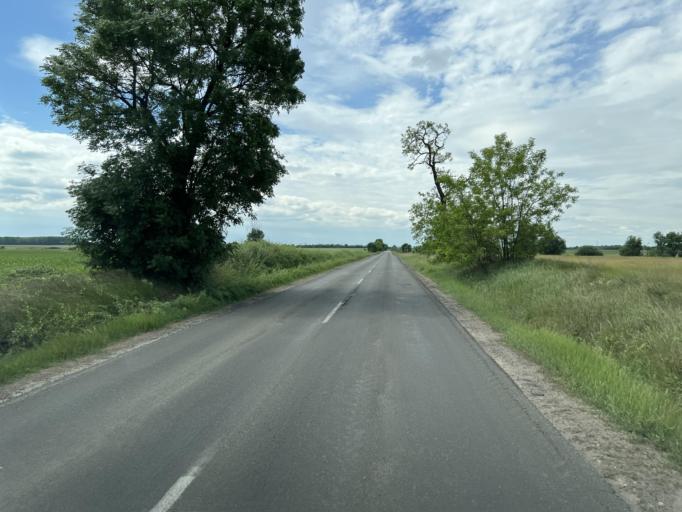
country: HU
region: Pest
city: Szentlorinckata
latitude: 47.5067
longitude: 19.7419
